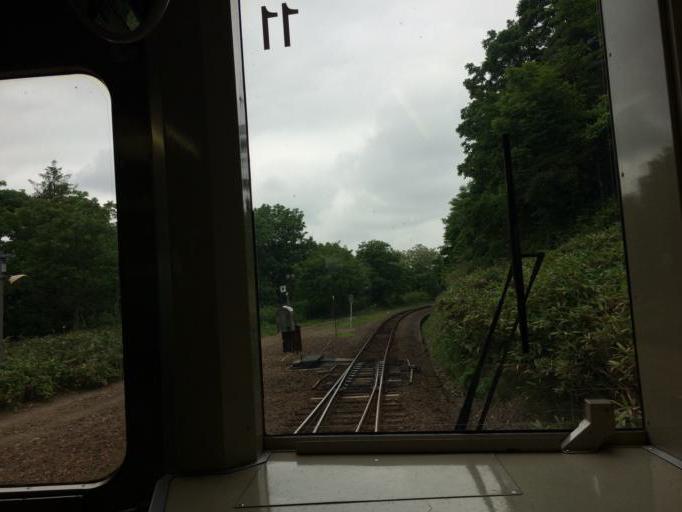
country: JP
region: Hokkaido
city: Iwanai
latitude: 42.9727
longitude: 140.6754
